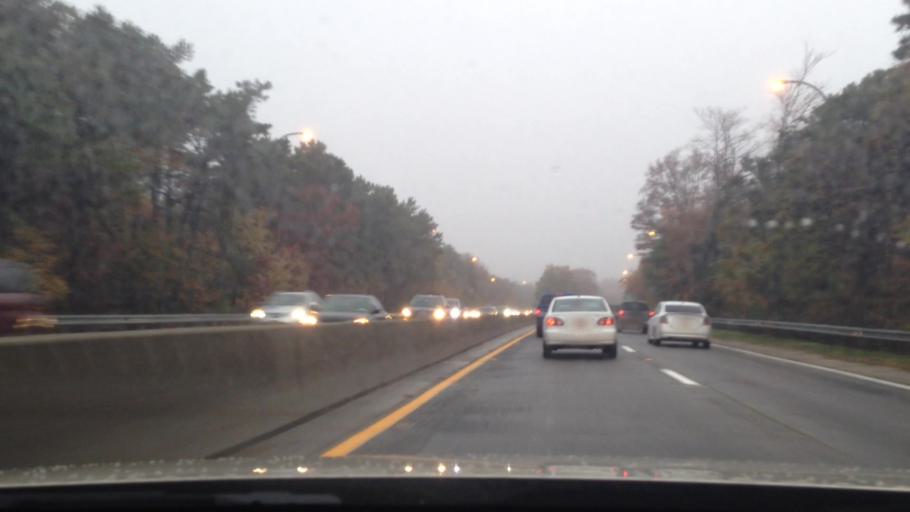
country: US
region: New York
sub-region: Suffolk County
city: Bay Wood
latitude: 40.7736
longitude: -73.2801
